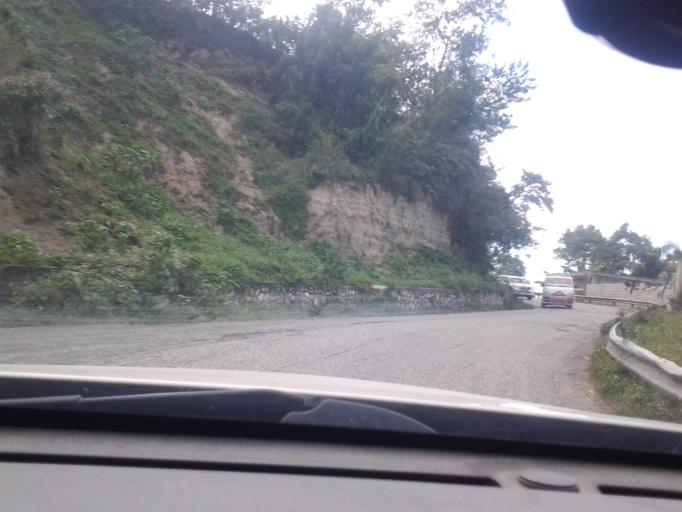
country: HT
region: Sud-Est
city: Jacmel
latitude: 18.3674
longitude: -72.5862
